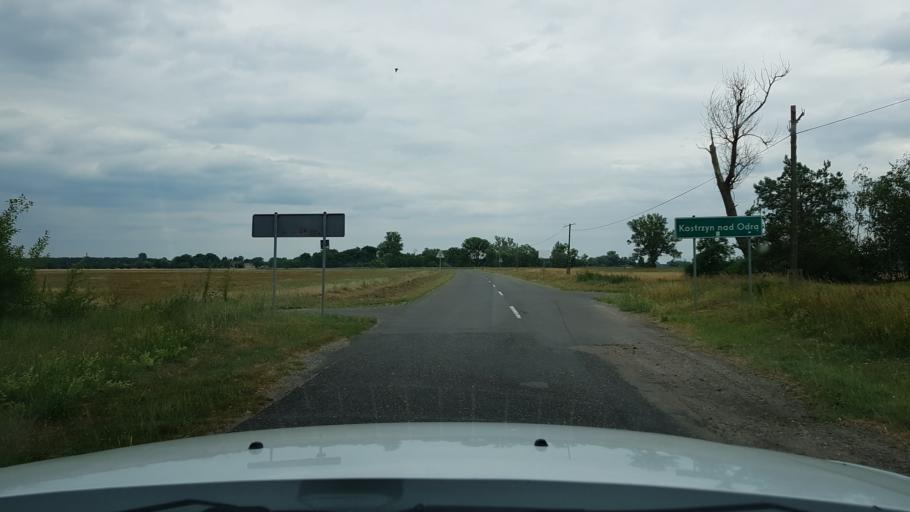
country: DE
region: Brandenburg
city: Manschnow
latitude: 52.6292
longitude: 14.5682
